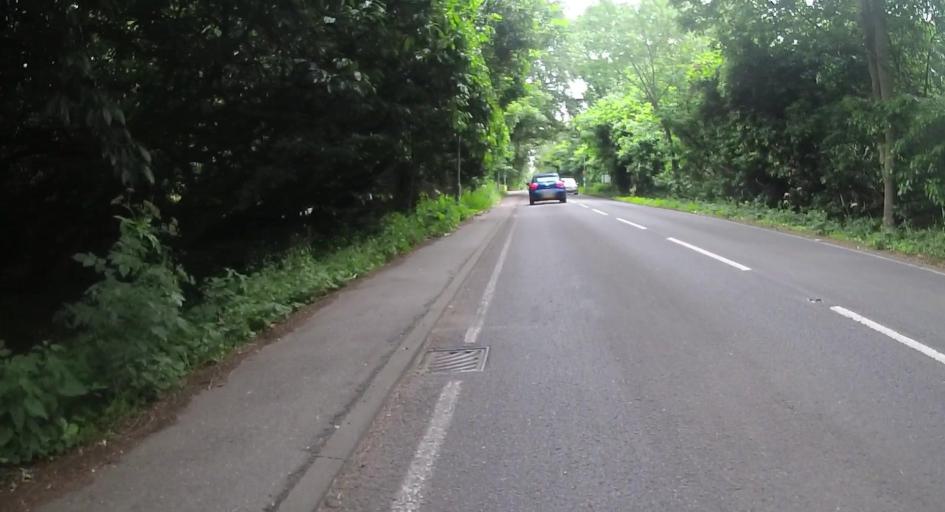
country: GB
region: England
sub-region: Wokingham
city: Winnersh
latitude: 51.4167
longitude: -0.8807
